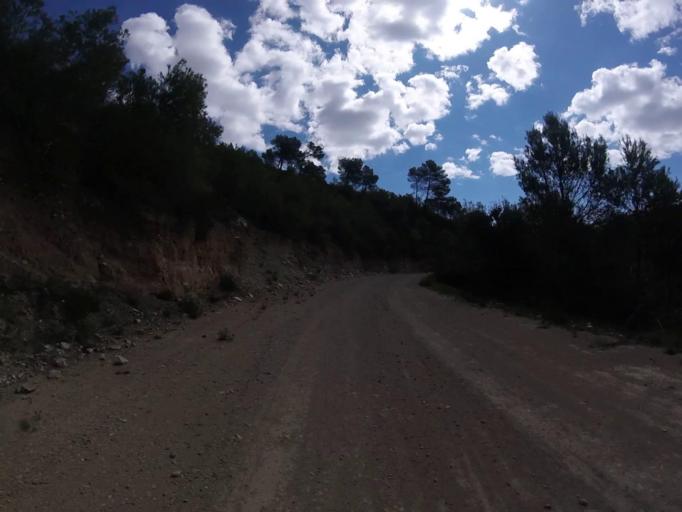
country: ES
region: Valencia
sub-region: Provincia de Castello
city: Santa Magdalena de Pulpis
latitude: 40.3111
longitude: 0.3197
